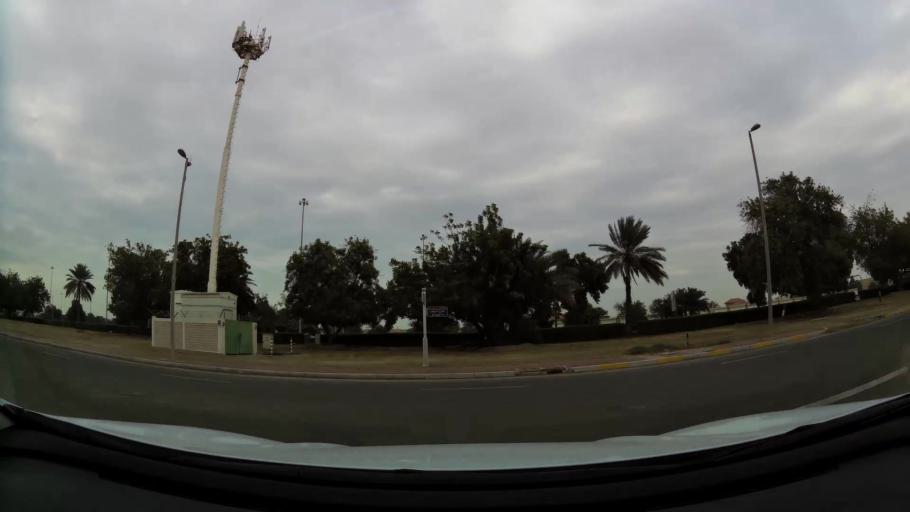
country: AE
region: Abu Dhabi
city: Abu Dhabi
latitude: 24.4323
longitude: 54.3785
